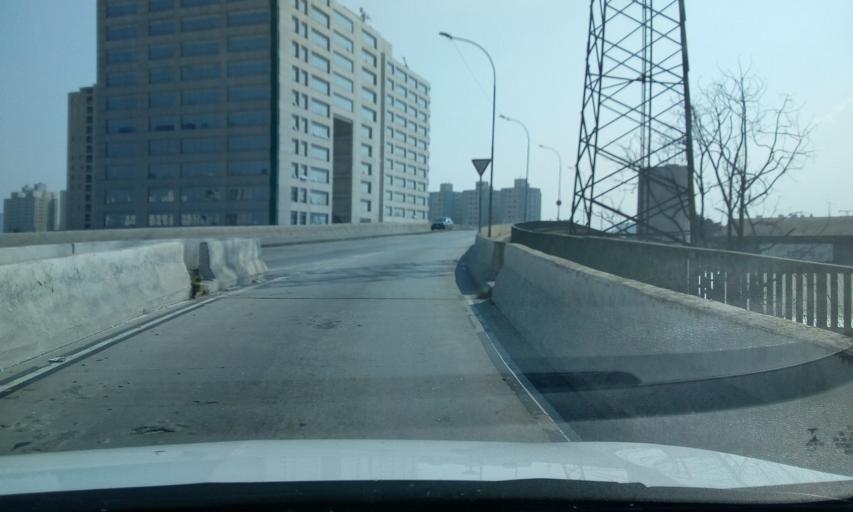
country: BR
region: Sao Paulo
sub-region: Sao Paulo
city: Sao Paulo
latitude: -23.5474
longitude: -46.6033
